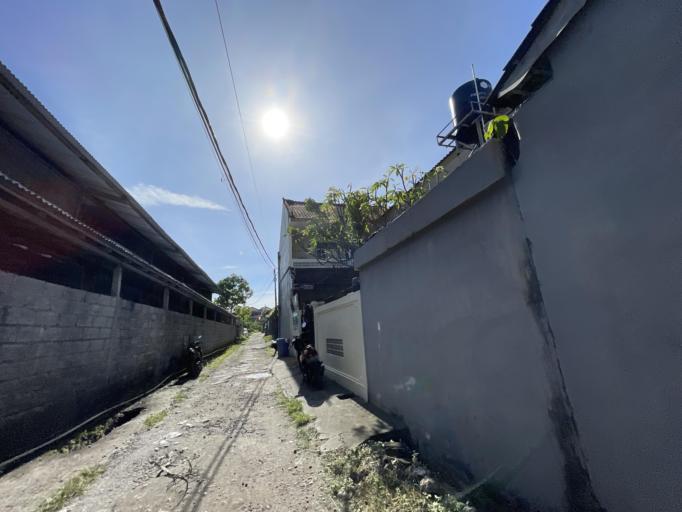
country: ID
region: Bali
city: Kuta
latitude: -8.6762
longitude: 115.1690
